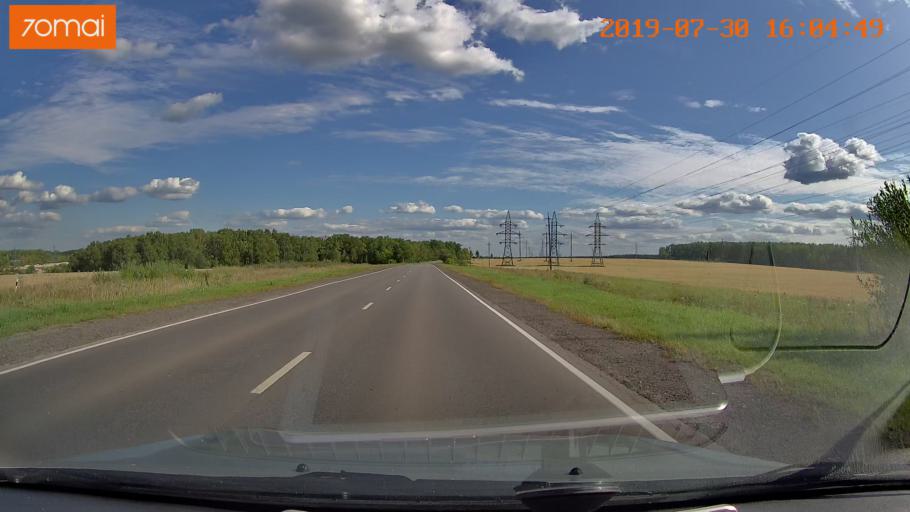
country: RU
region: Moskovskaya
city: Lopatinskiy
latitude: 55.2755
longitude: 38.7112
